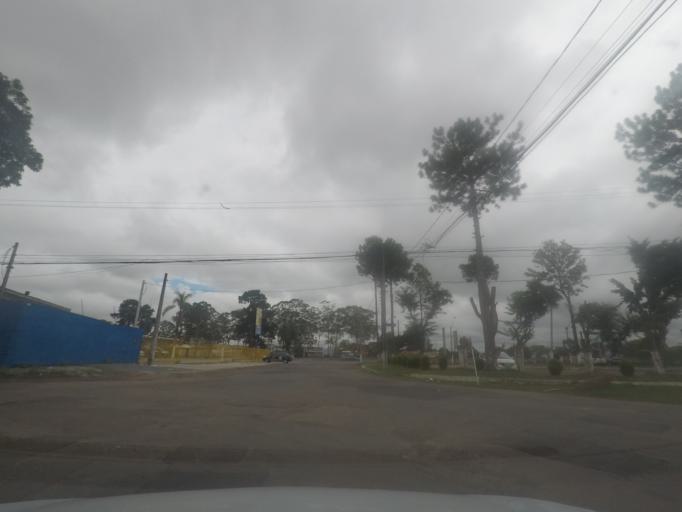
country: BR
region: Parana
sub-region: Pinhais
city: Pinhais
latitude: -25.4483
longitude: -49.2287
